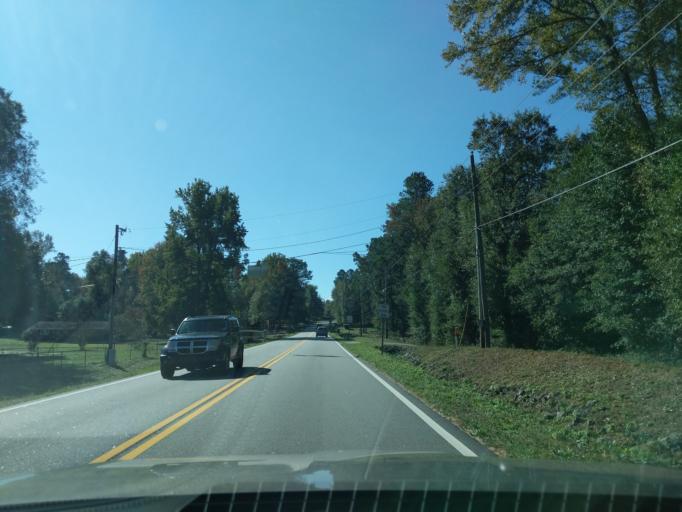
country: US
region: Georgia
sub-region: Richmond County
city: Hephzibah
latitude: 33.3366
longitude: -82.0073
